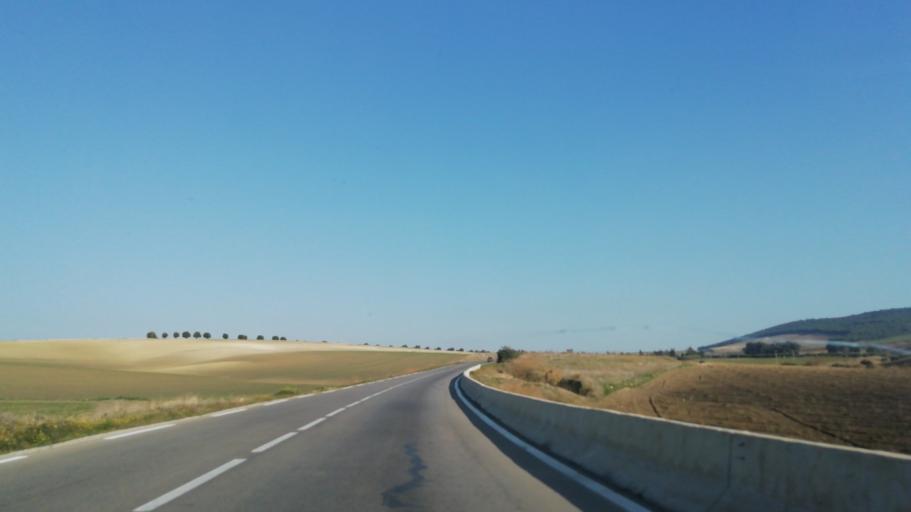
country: DZ
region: Ain Temouchent
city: Hammam Bou Hadjar
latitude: 35.1698
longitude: -0.9068
